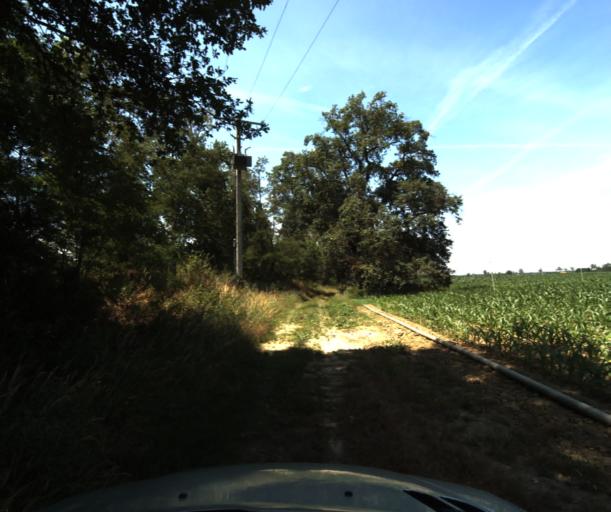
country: FR
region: Midi-Pyrenees
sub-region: Departement de la Haute-Garonne
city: Labastidette
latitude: 43.4615
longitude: 1.2248
